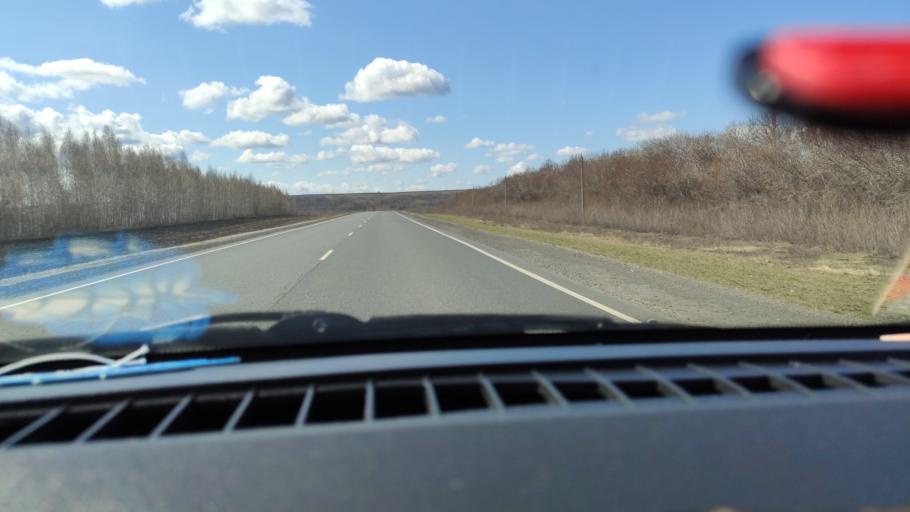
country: RU
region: Samara
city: Syzran'
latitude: 52.9755
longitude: 48.3096
